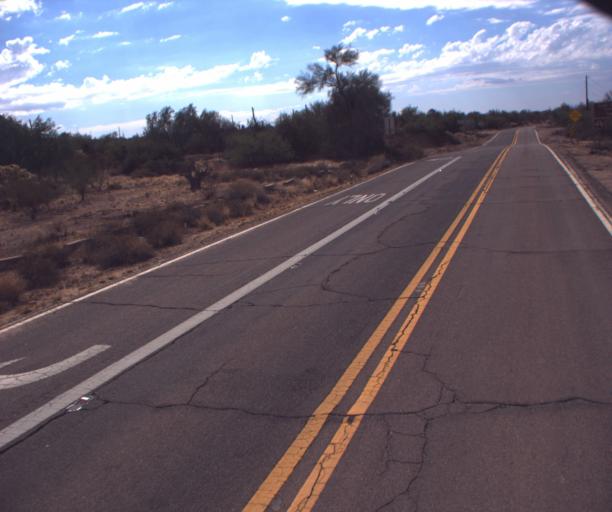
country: US
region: Arizona
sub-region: Pinal County
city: Apache Junction
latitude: 33.4676
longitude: -111.4789
